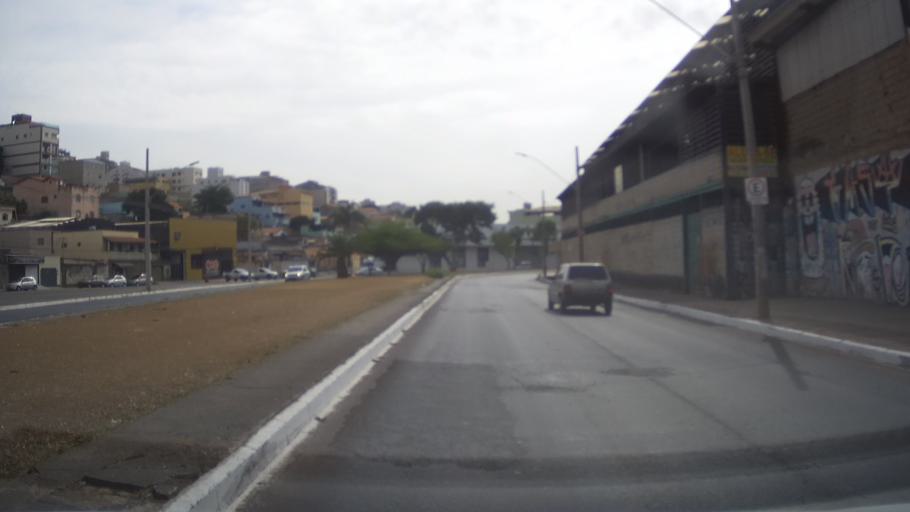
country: BR
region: Minas Gerais
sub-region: Contagem
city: Contagem
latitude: -19.9499
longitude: -44.0376
